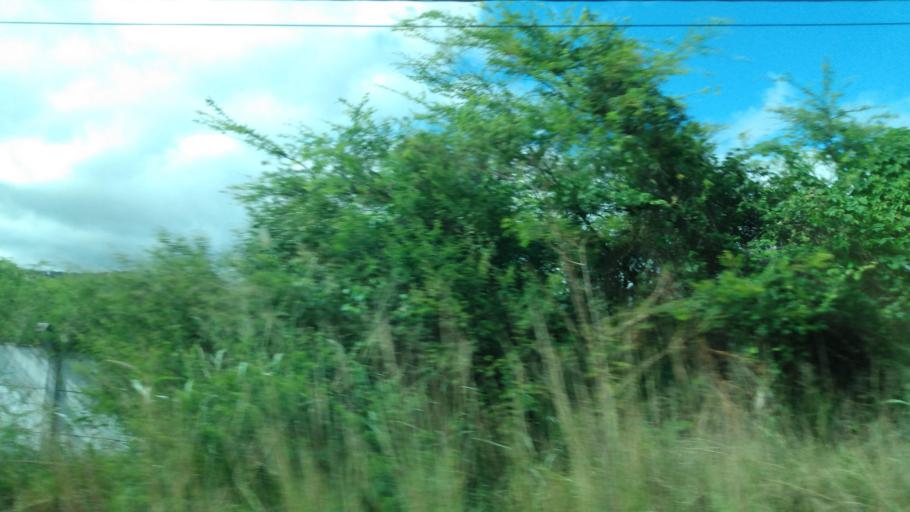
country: BR
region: Pernambuco
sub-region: Caruaru
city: Caruaru
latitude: -8.3023
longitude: -36.0012
